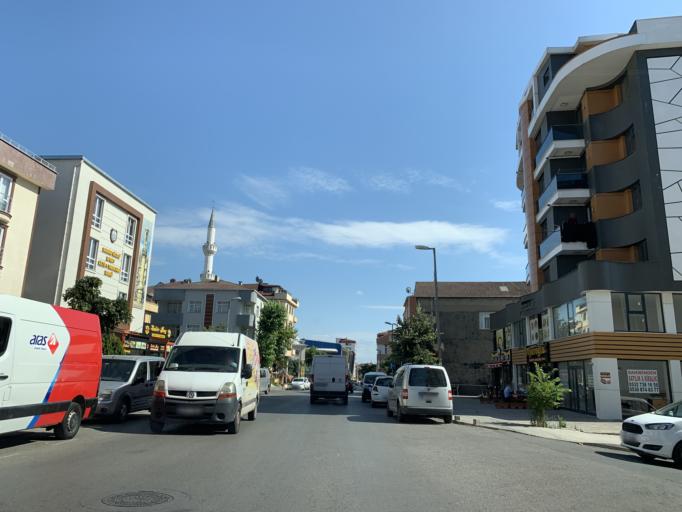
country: TR
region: Istanbul
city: Pendik
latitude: 40.8828
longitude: 29.2725
